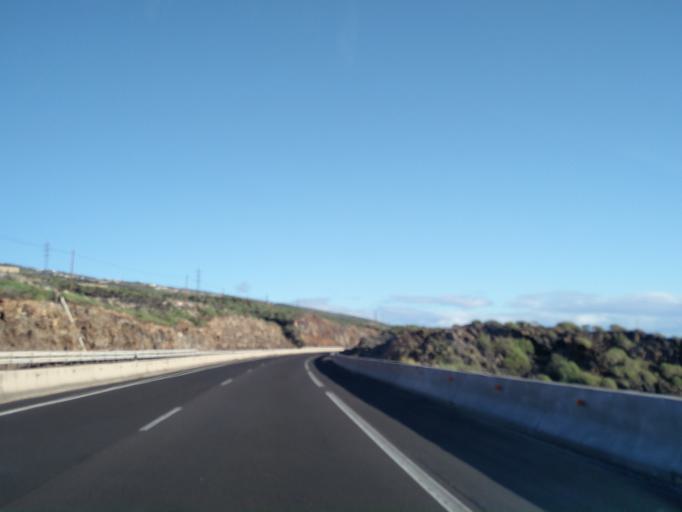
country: ES
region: Canary Islands
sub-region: Provincia de Santa Cruz de Tenerife
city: Fasnia
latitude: 28.2339
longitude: -16.4085
